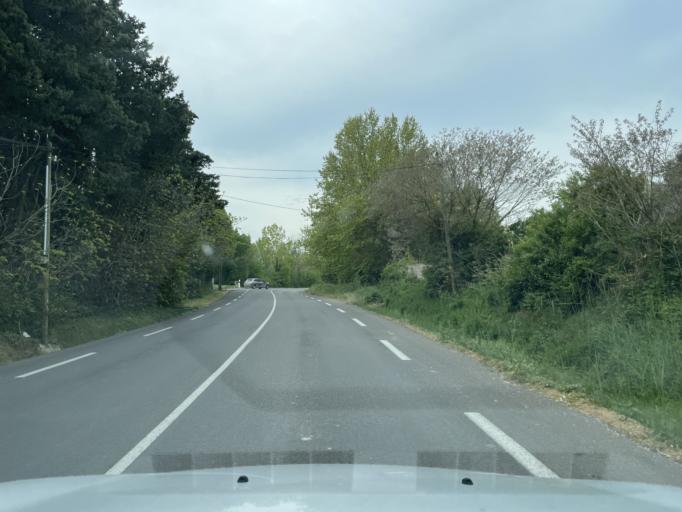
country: FR
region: Provence-Alpes-Cote d'Azur
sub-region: Departement des Bouches-du-Rhone
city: Tarascon
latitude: 43.8186
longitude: 4.6830
